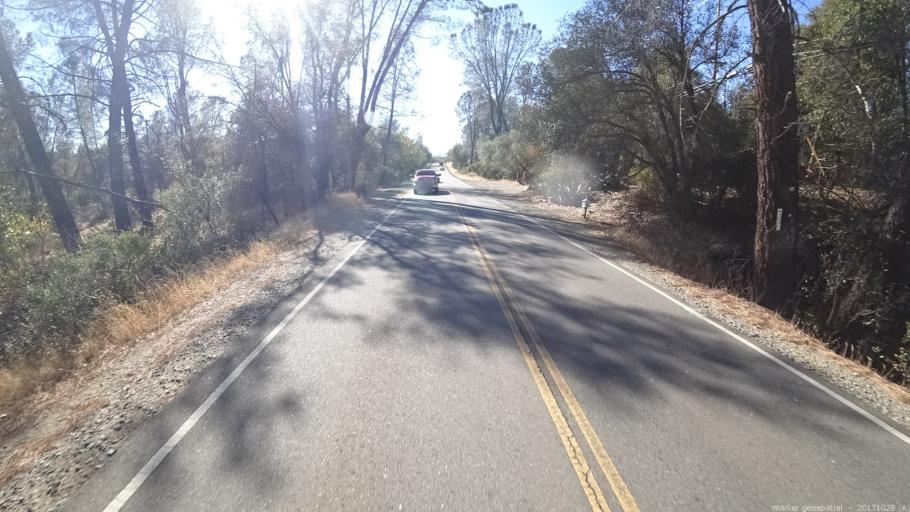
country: US
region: California
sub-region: Shasta County
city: Redding
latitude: 40.6233
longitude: -122.4206
